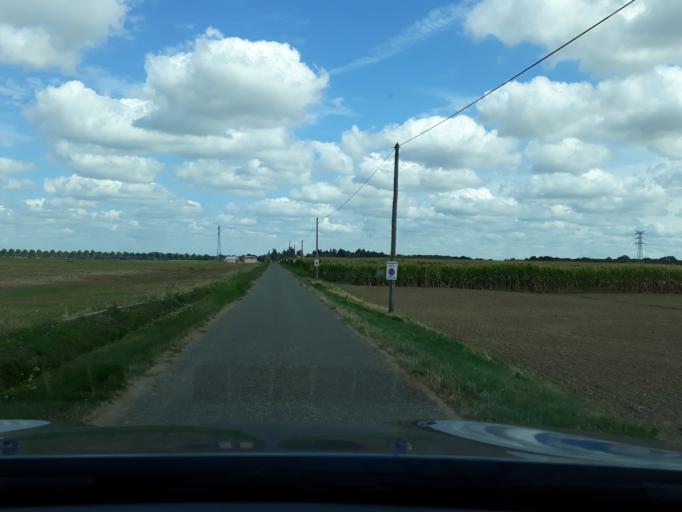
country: FR
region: Centre
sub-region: Departement du Loiret
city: Saint-Cyr-en-Val
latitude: 47.8369
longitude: 1.9773
